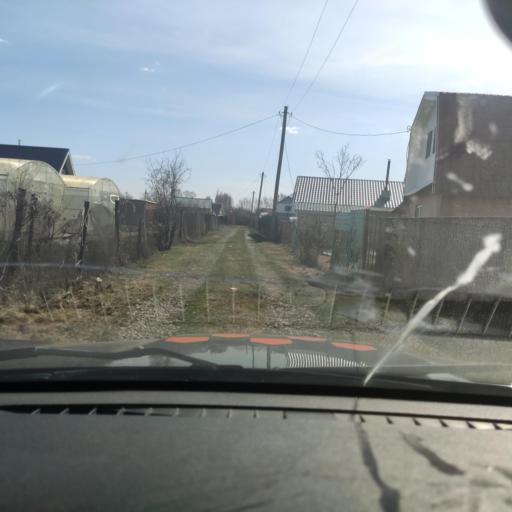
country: RU
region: Samara
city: Tol'yatti
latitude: 53.7039
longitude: 49.4119
